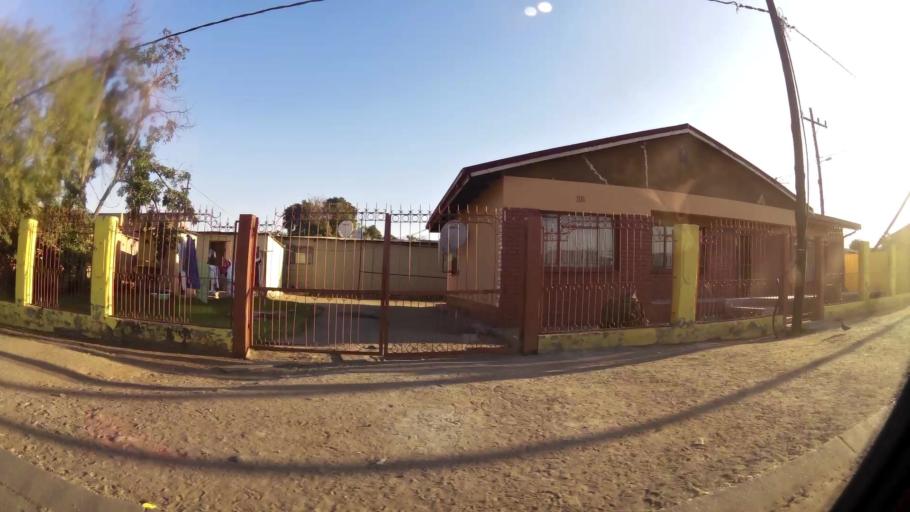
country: ZA
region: North-West
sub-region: Bojanala Platinum District Municipality
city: Rustenburg
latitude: -25.6385
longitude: 27.2180
